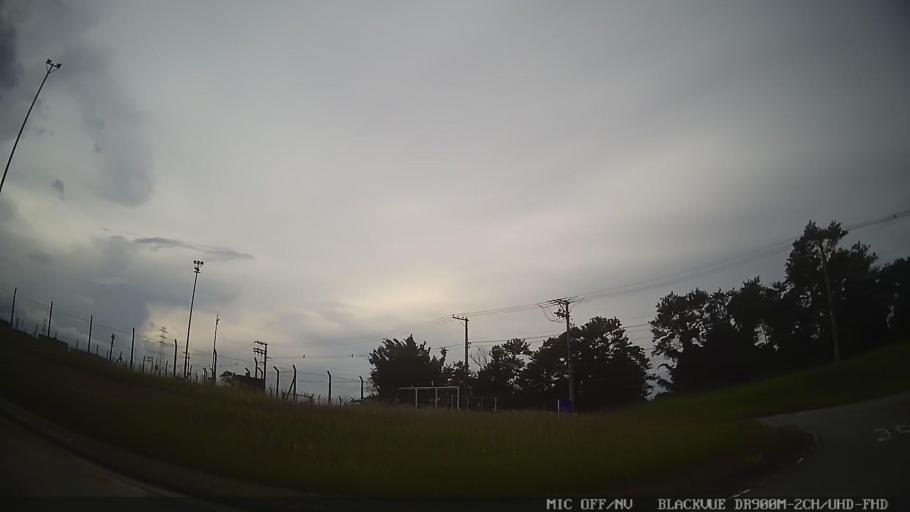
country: BR
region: Sao Paulo
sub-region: Aruja
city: Aruja
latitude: -23.4391
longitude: -46.2557
